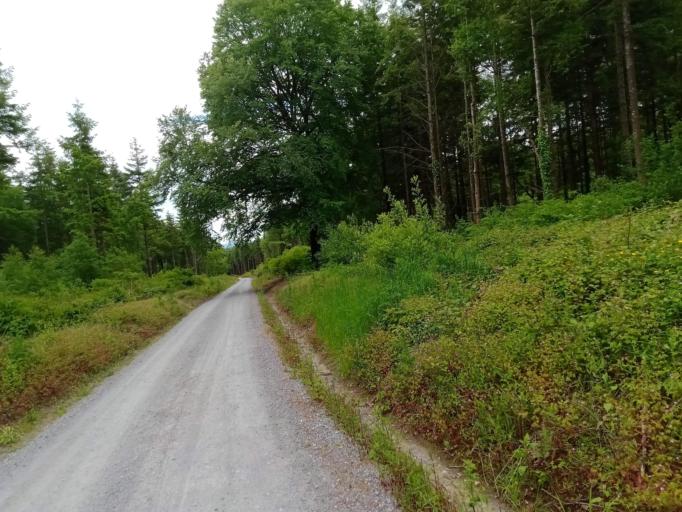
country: IE
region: Leinster
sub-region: Kilkenny
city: Thomastown
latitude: 52.4700
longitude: -7.0504
